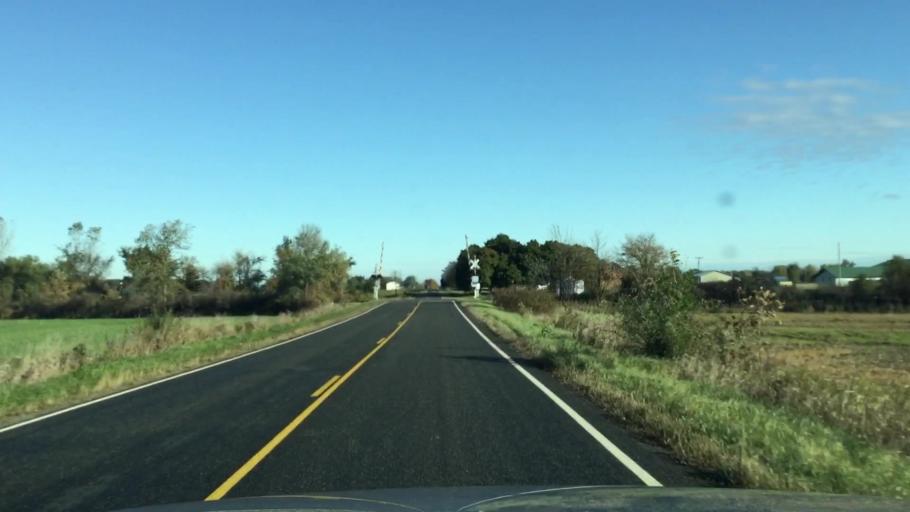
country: US
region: Michigan
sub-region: Shiawassee County
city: Durand
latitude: 42.8903
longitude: -83.9477
